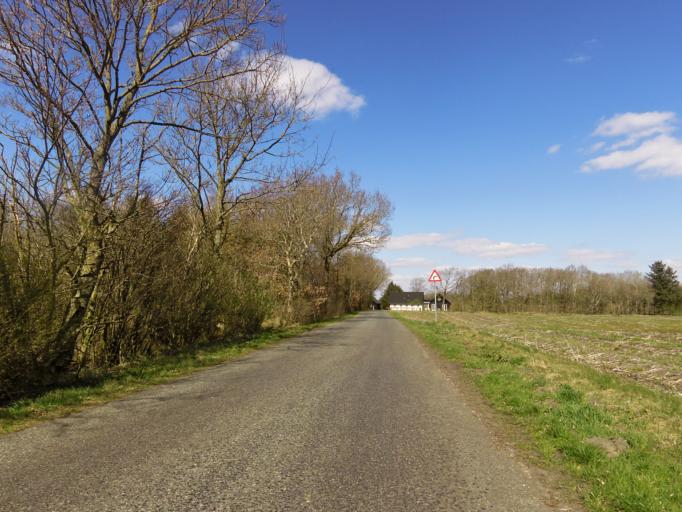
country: DK
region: South Denmark
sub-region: Esbjerg Kommune
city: Ribe
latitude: 55.3440
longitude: 8.8312
